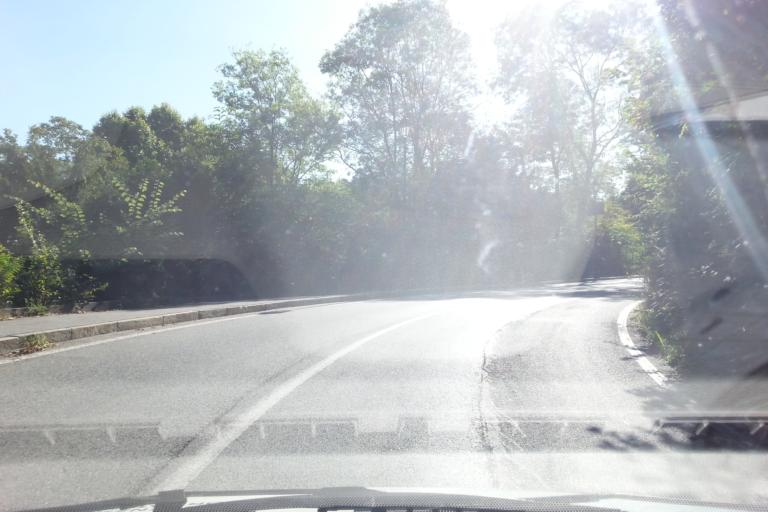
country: IT
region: Piedmont
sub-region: Provincia di Torino
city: Turin
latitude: 45.0593
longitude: 7.7056
